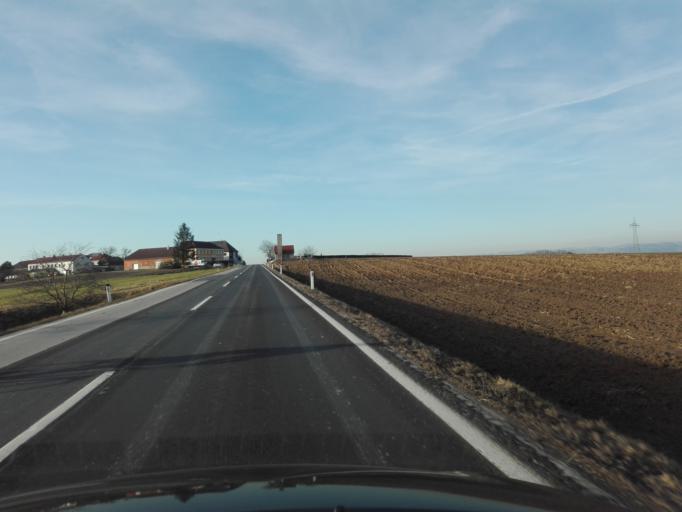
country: AT
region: Lower Austria
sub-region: Politischer Bezirk Amstetten
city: Strengberg
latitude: 48.1560
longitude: 14.6209
